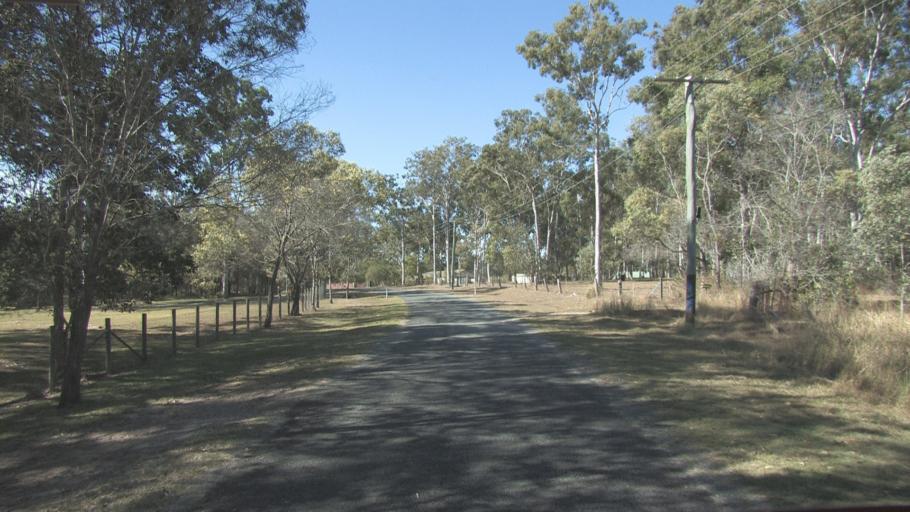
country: AU
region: Queensland
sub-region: Logan
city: Park Ridge South
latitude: -27.7247
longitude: 152.9715
